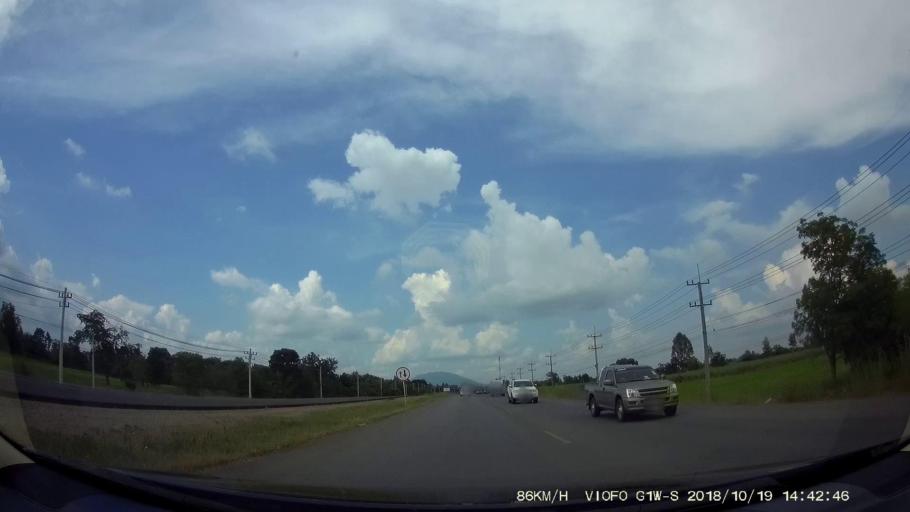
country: TH
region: Chaiyaphum
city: Phu Khiao
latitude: 16.2722
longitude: 102.2044
